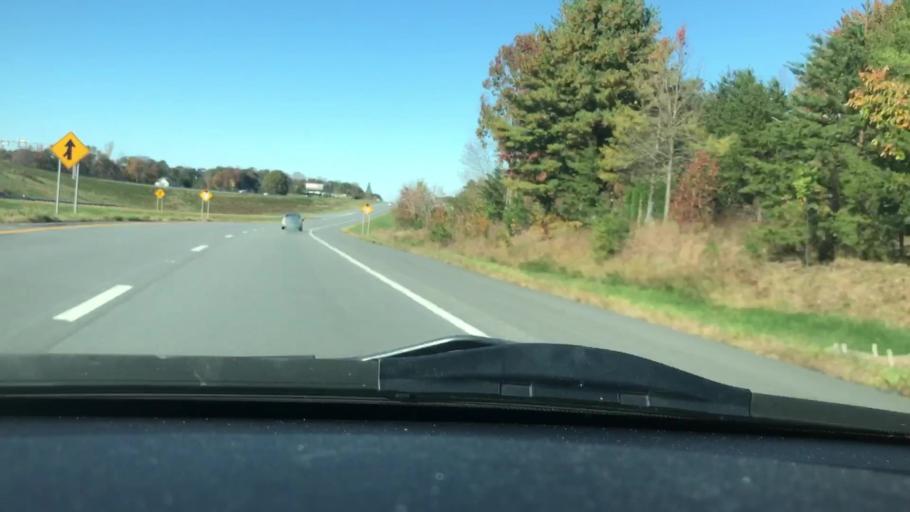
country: US
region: North Carolina
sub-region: Guilford County
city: Stokesdale
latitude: 36.2839
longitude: -79.9391
